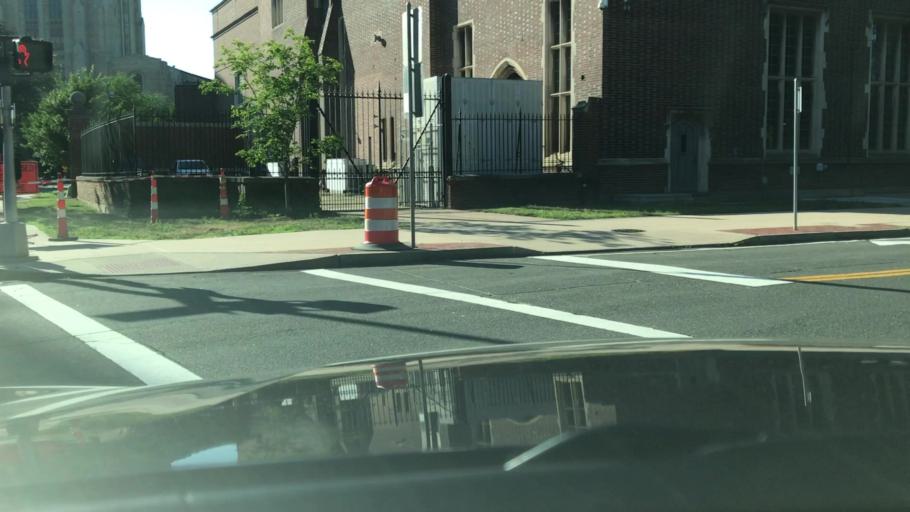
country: US
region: Connecticut
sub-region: New Haven County
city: New Haven
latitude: 41.3125
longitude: -72.9286
